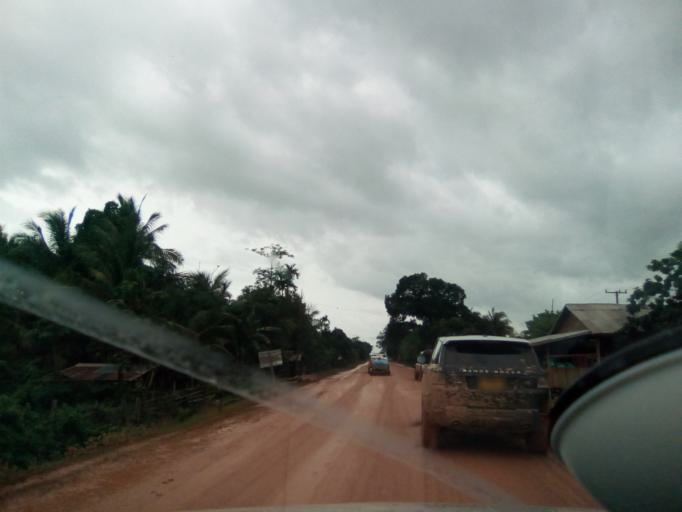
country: LA
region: Attapu
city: Attapu
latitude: 14.7632
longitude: 106.7143
